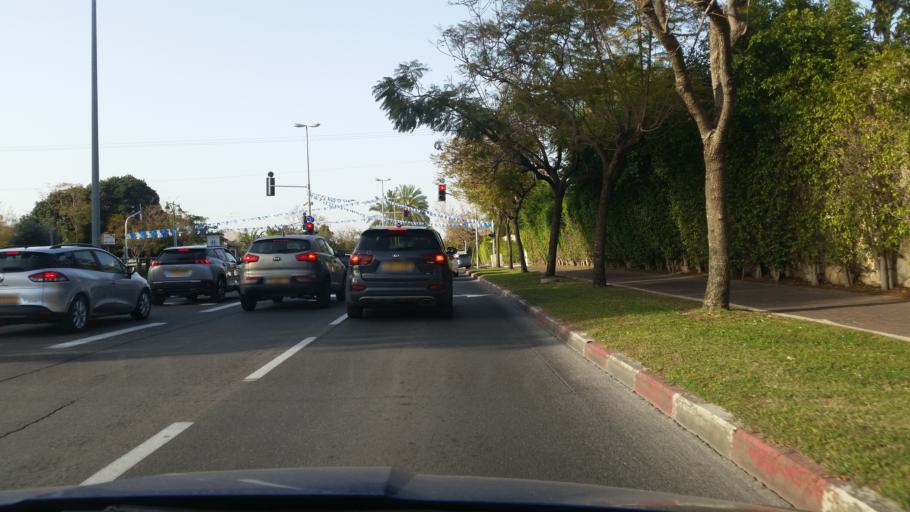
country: IL
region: Central District
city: Ra'anana
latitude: 32.1893
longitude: 34.8551
